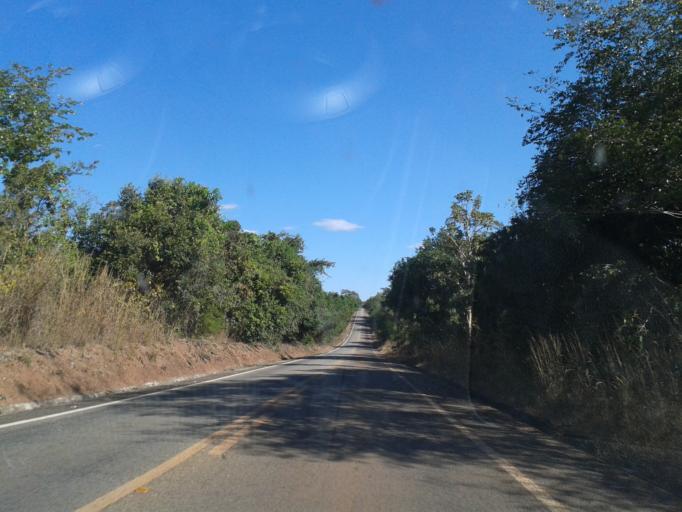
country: BR
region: Goias
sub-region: Mozarlandia
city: Mozarlandia
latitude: -14.4289
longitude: -50.4539
